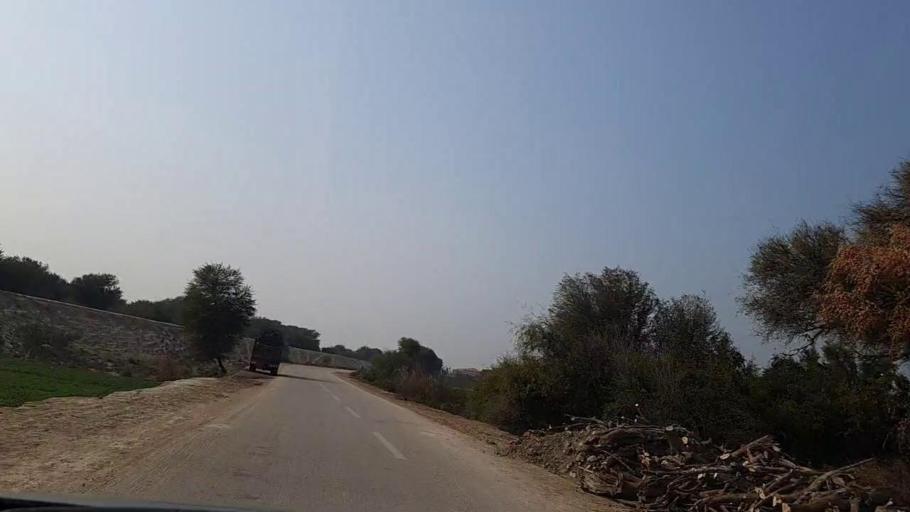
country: PK
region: Sindh
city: Sann
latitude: 26.1479
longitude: 68.1330
